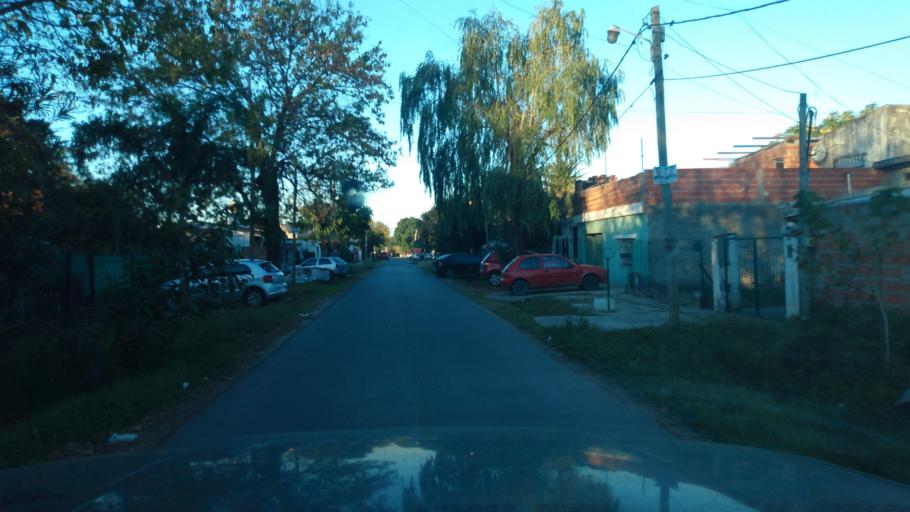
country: AR
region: Buenos Aires
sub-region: Partido de Merlo
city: Merlo
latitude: -34.6573
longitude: -58.7484
